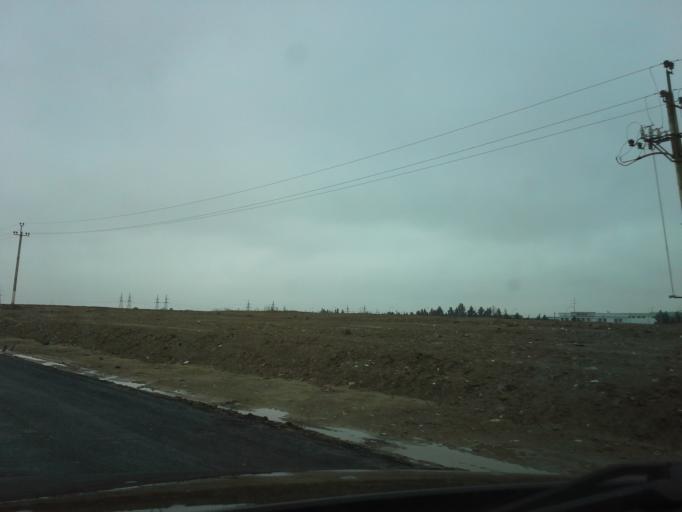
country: TM
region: Ahal
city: Ashgabat
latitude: 37.9548
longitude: 58.4314
